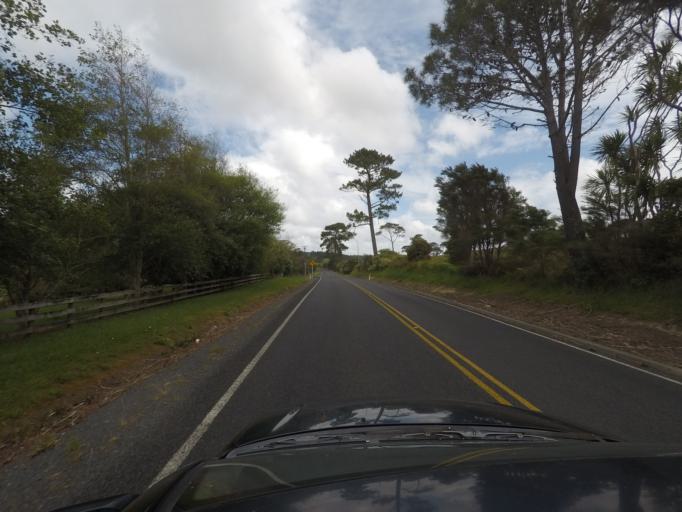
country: NZ
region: Auckland
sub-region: Auckland
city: Parakai
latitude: -36.6523
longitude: 174.5213
